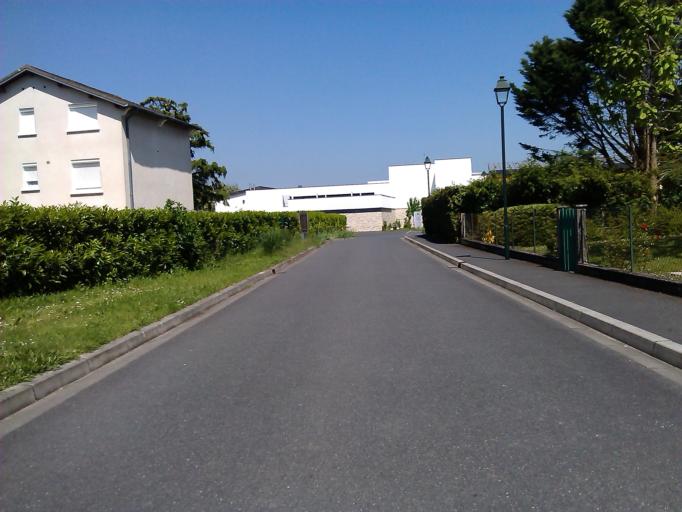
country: FR
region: Centre
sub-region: Departement de l'Indre
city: Argenton-sur-Creuse
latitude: 46.5911
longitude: 1.5272
